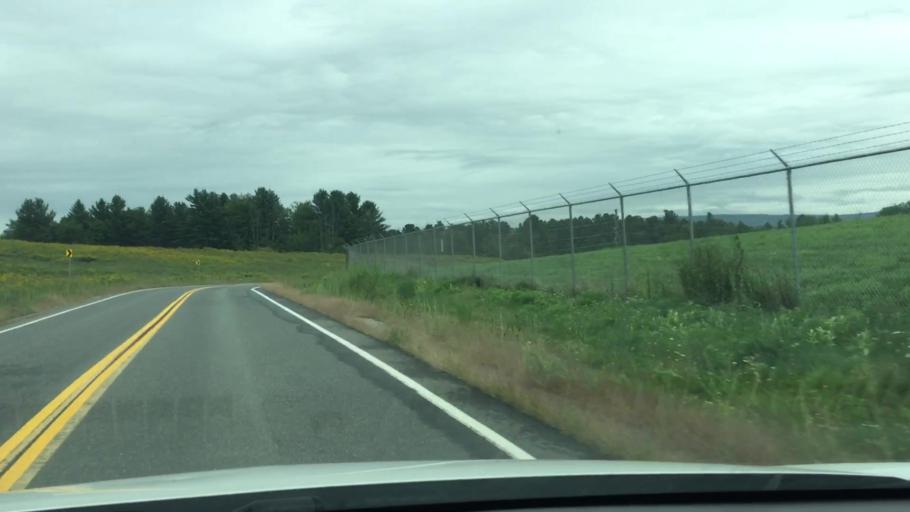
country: US
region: Massachusetts
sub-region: Berkshire County
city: Pittsfield
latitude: 42.4331
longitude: -73.2800
